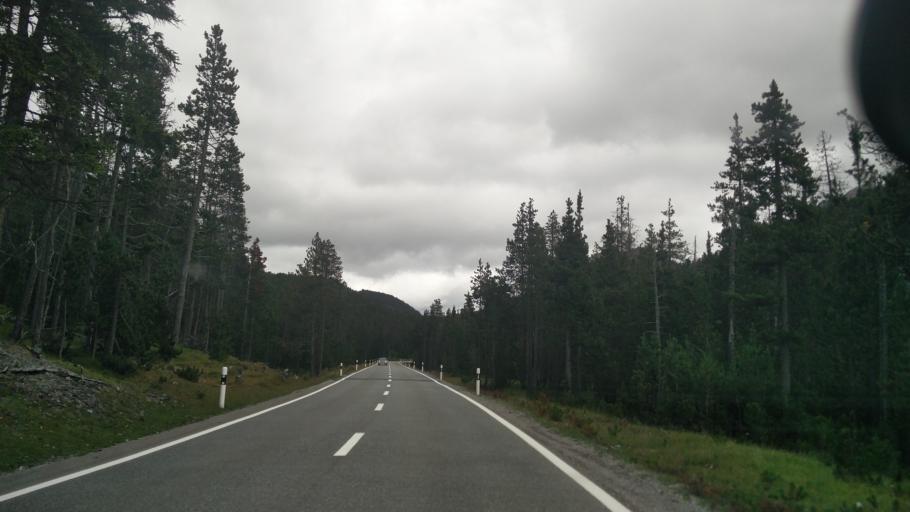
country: CH
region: Grisons
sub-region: Inn District
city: Scuol
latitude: 46.6520
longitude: 10.2587
